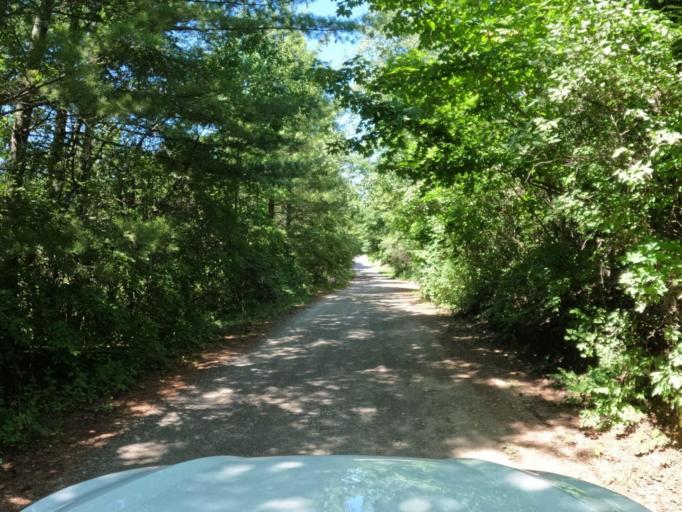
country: CA
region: Ontario
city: Cambridge
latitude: 43.4098
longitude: -80.2545
